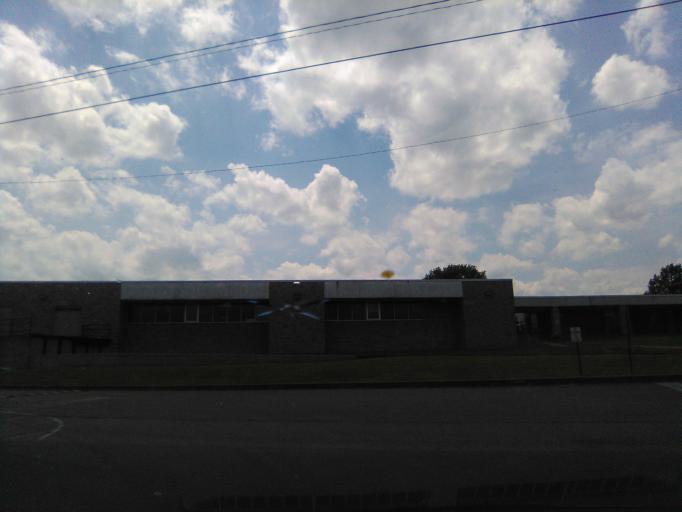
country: US
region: Tennessee
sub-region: Davidson County
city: Belle Meade
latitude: 36.1318
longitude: -86.8556
